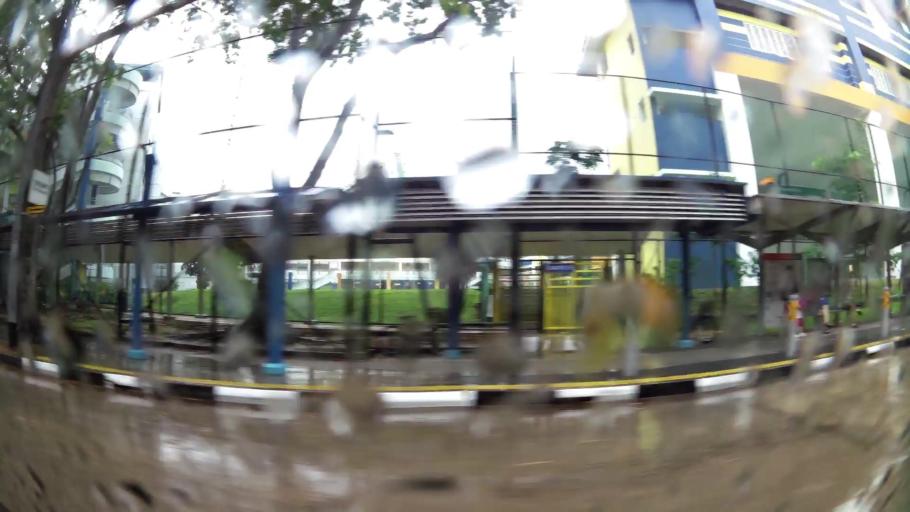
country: MY
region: Johor
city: Kampung Pasir Gudang Baru
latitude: 1.3872
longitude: 103.9041
